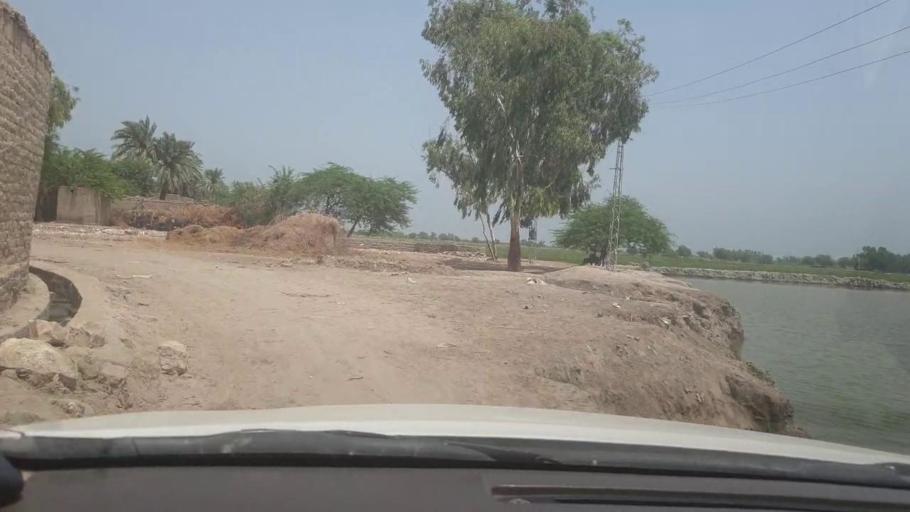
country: PK
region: Sindh
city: Shikarpur
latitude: 27.9488
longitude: 68.5724
